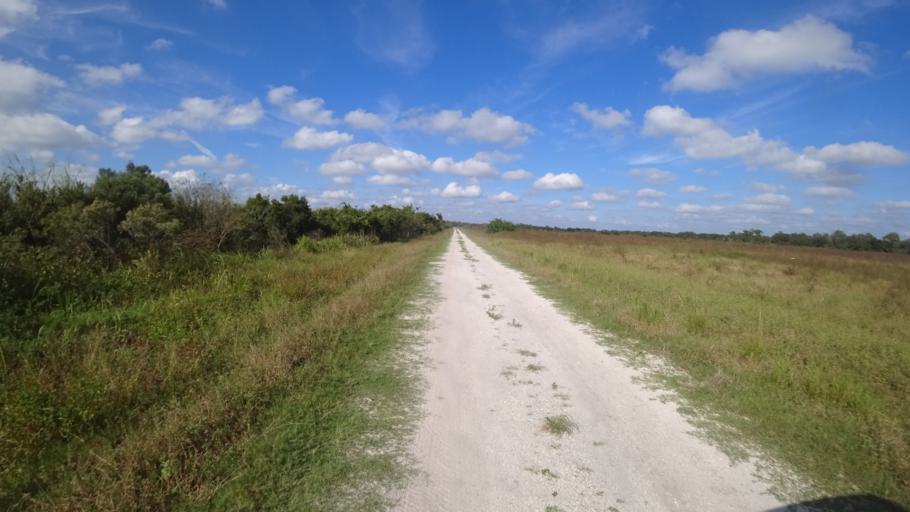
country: US
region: Florida
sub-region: Sarasota County
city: Lake Sarasota
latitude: 27.3655
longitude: -82.1574
